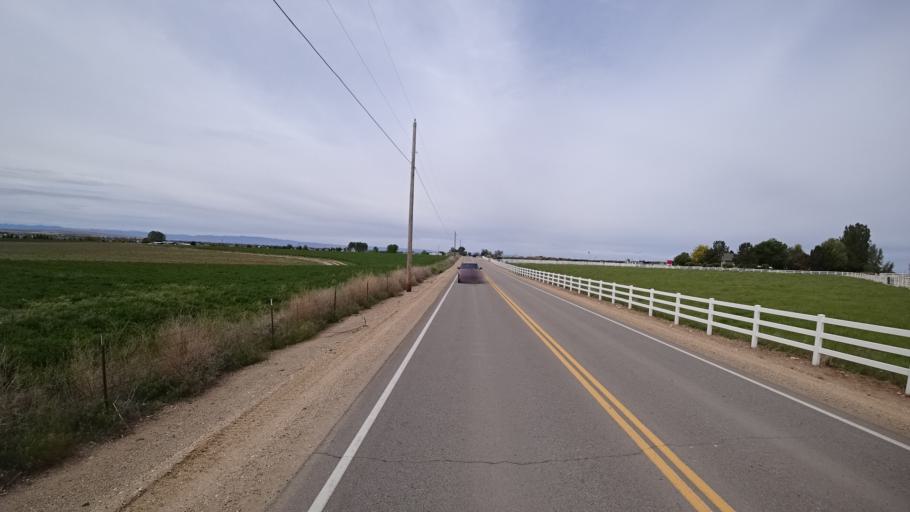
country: US
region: Idaho
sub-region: Ada County
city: Kuna
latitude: 43.5318
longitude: -116.3674
